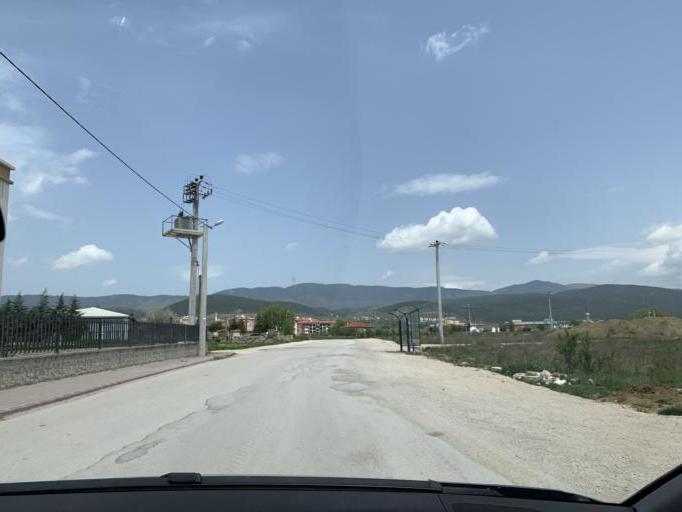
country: TR
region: Bolu
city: Bolu
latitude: 40.7348
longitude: 31.5641
